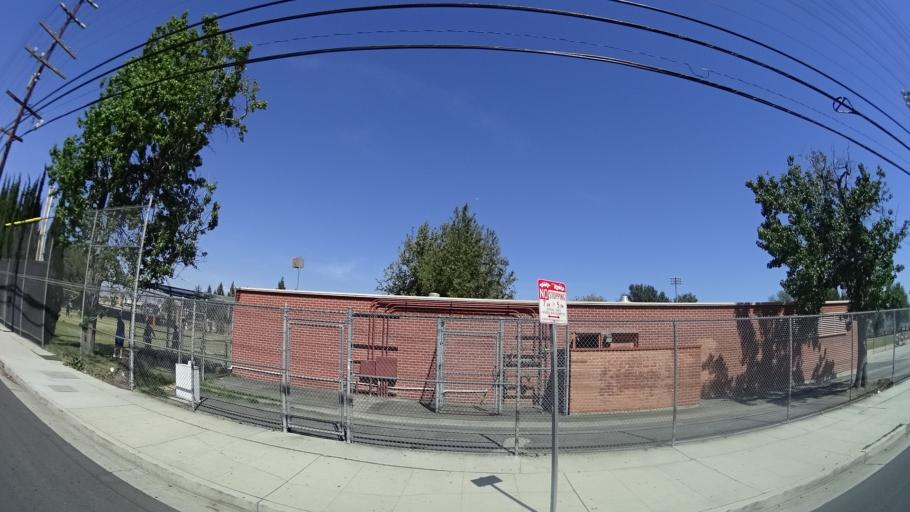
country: US
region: California
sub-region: Los Angeles County
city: Van Nuys
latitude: 34.1773
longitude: -118.4181
